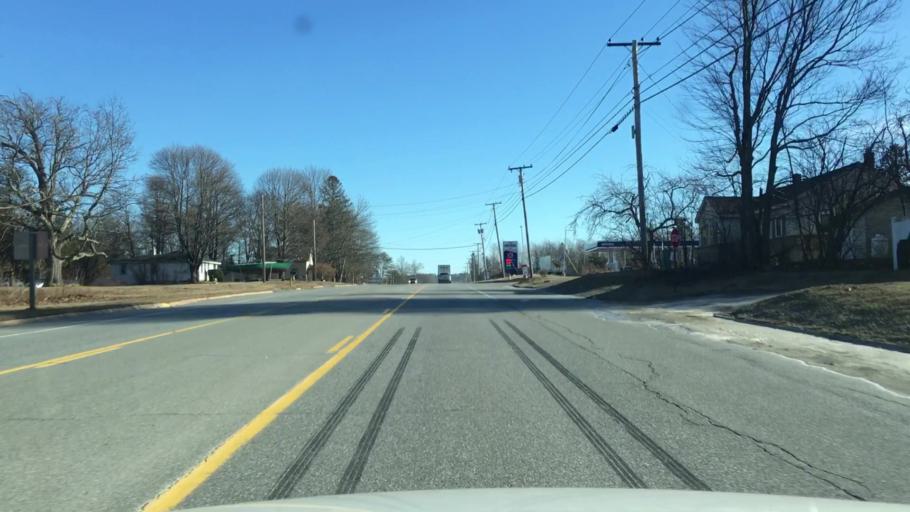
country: US
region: Maine
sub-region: Penobscot County
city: Holden
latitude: 44.7654
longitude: -68.7076
